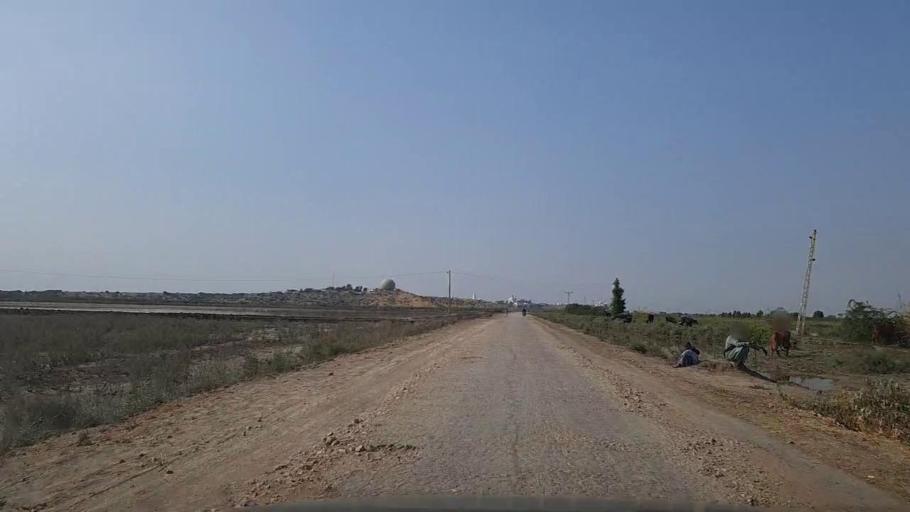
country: PK
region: Sindh
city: Chuhar Jamali
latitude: 24.5494
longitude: 67.8964
